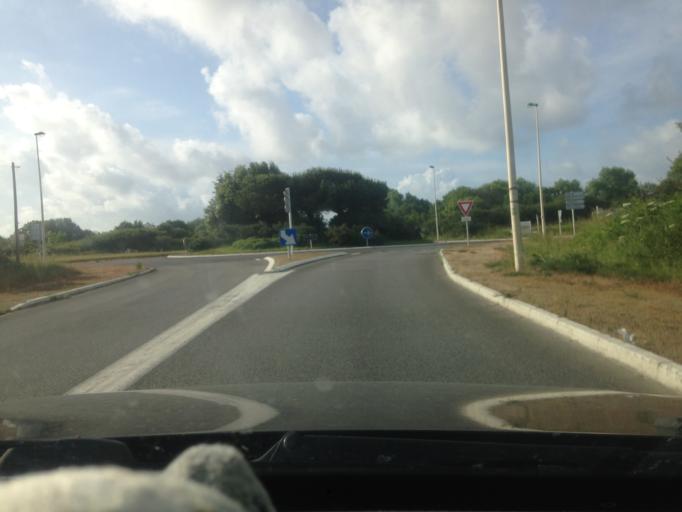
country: FR
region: Brittany
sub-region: Departement du Morbihan
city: Erdeven
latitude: 47.6211
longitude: -3.1357
